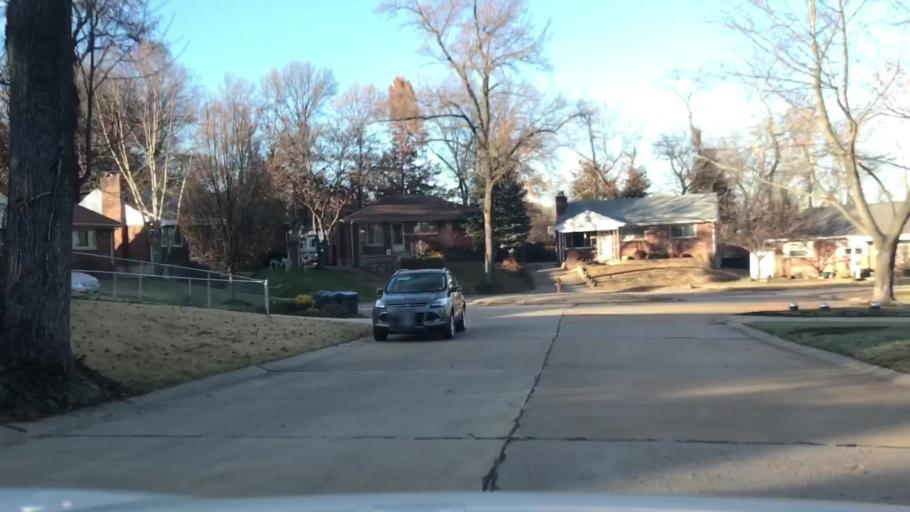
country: US
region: Missouri
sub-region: Saint Louis County
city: Brentwood
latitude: 38.6199
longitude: -90.3428
